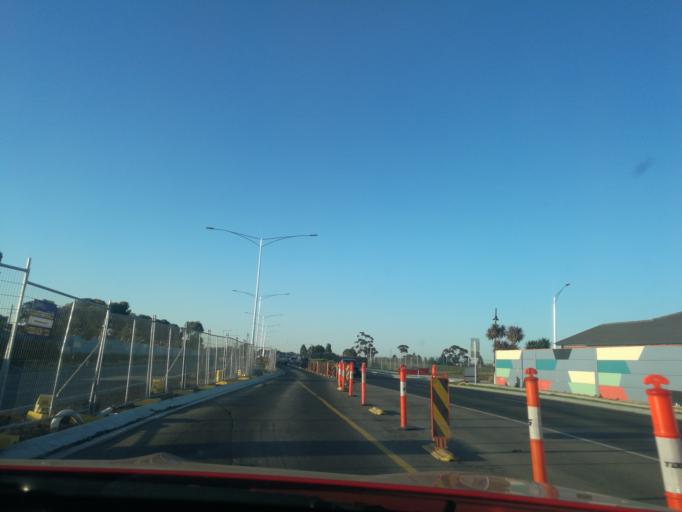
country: AU
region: Victoria
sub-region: Wyndham
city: Williams Landing
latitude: -37.8828
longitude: 144.7475
